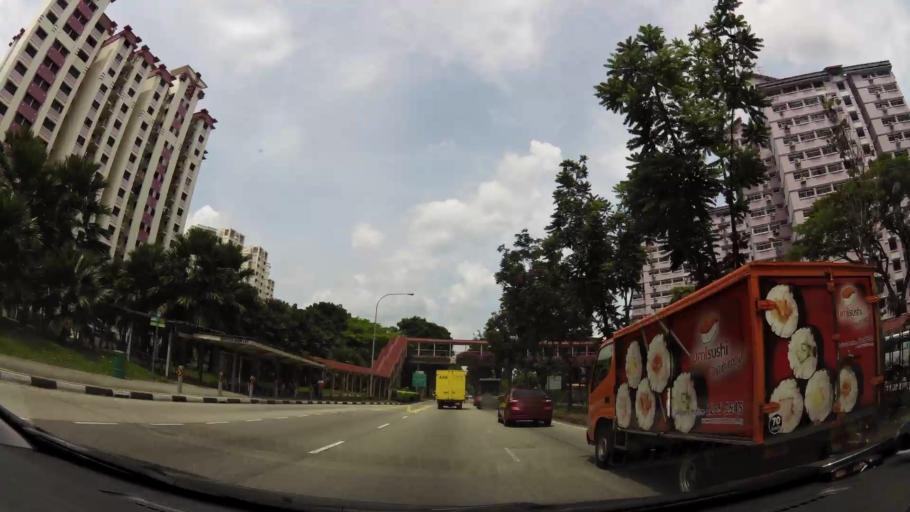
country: MY
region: Johor
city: Johor Bahru
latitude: 1.3451
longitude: 103.7063
